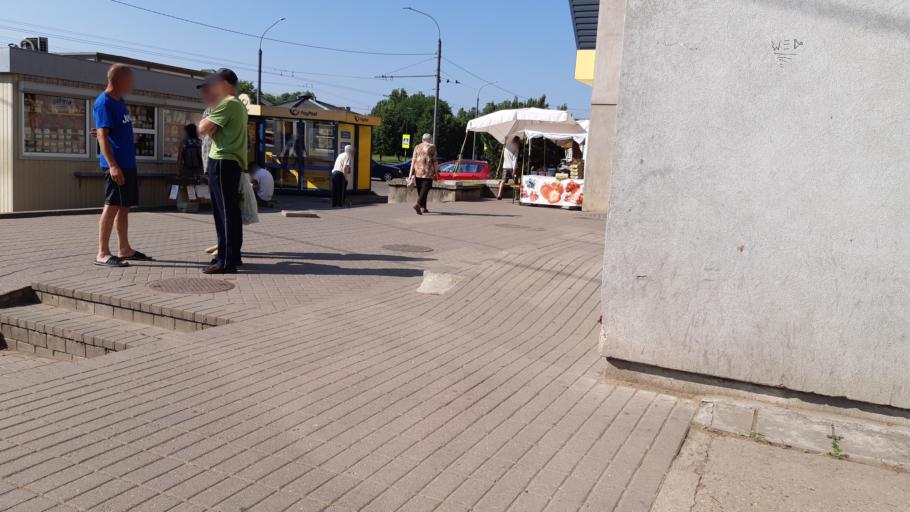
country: LT
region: Kauno apskritis
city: Dainava (Kaunas)
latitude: 54.9251
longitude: 23.9829
